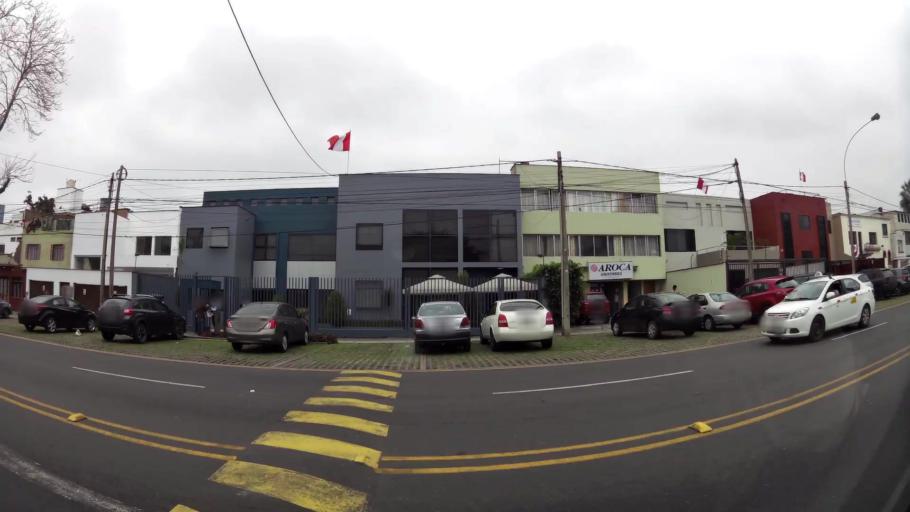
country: PE
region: Lima
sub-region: Lima
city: Surco
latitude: -12.1287
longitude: -77.0180
